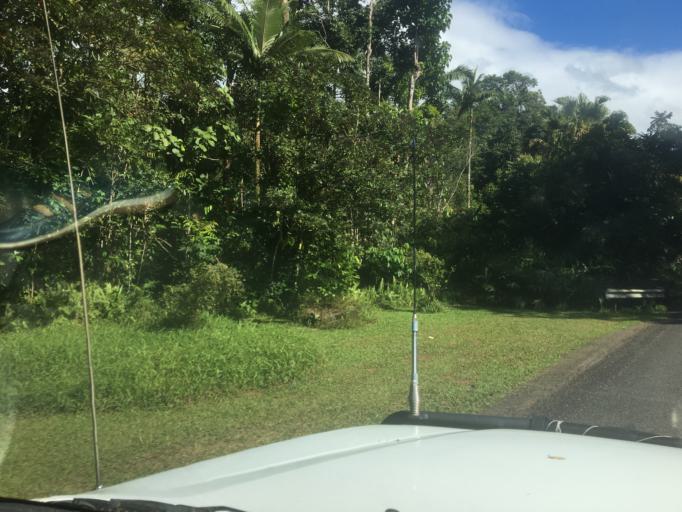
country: AU
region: Queensland
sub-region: Cassowary Coast
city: Innisfail
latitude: -17.3476
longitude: 145.8782
